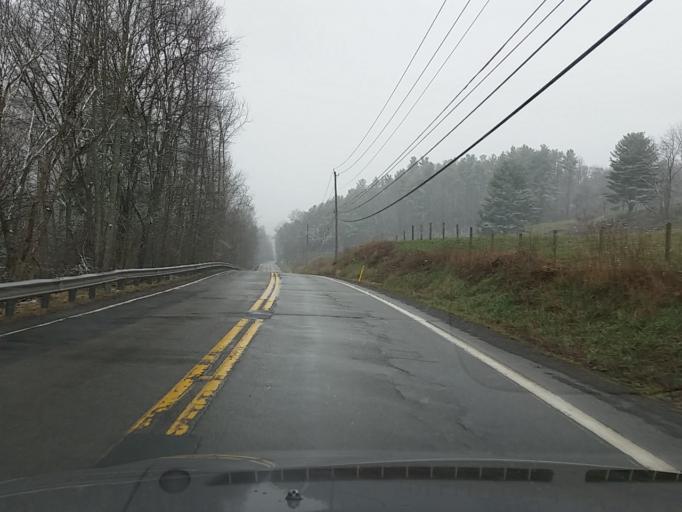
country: US
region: Pennsylvania
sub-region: Luzerne County
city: East Berwick
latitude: 41.1951
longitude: -76.2563
